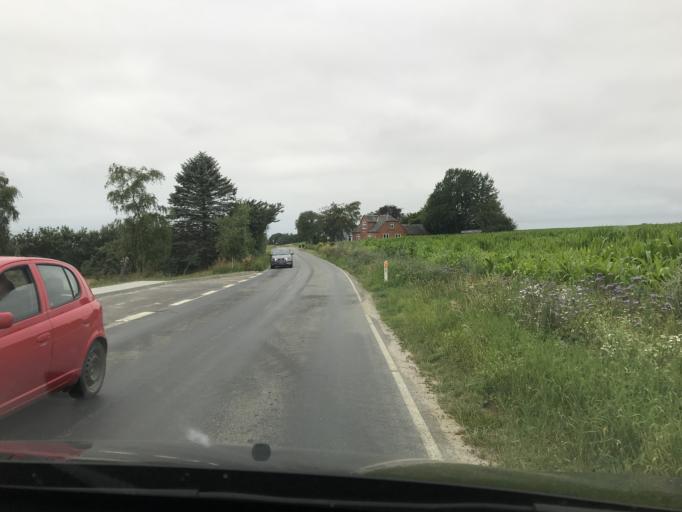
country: DK
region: South Denmark
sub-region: AEro Kommune
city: AEroskobing
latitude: 54.8489
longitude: 10.4190
